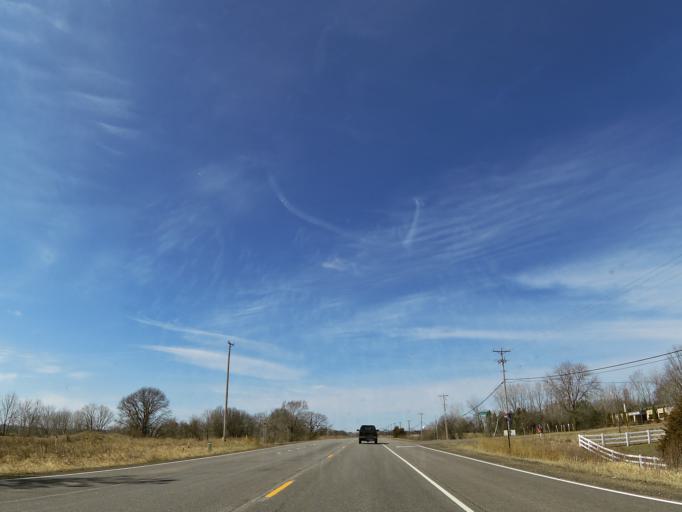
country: US
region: Minnesota
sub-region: Washington County
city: Lake Elmo
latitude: 44.9966
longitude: -92.8975
